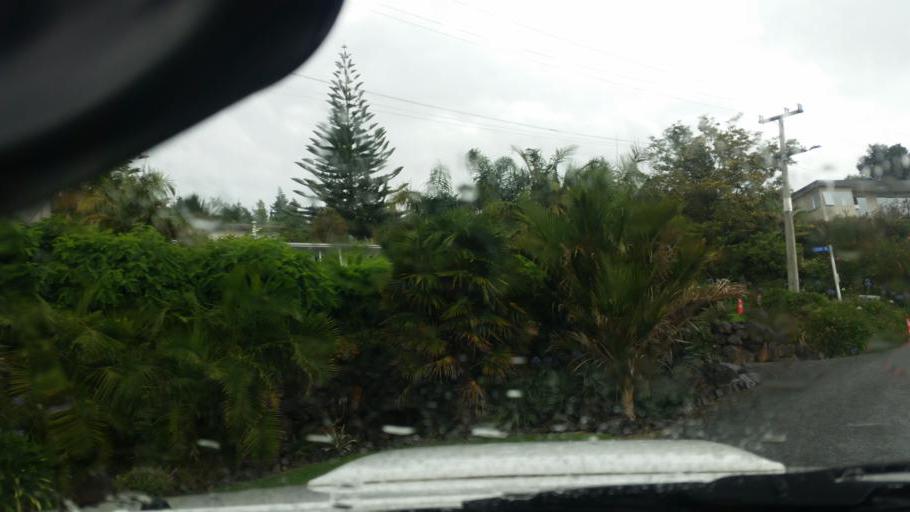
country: NZ
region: Auckland
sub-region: Auckland
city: Wellsford
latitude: -36.1574
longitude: 174.2279
